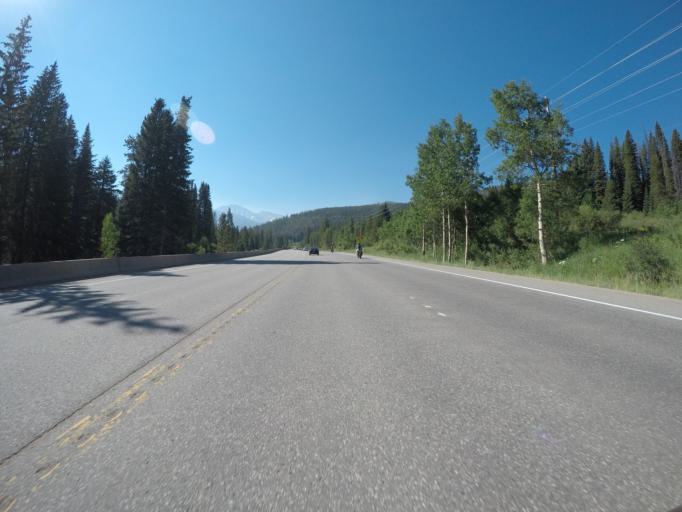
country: US
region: Colorado
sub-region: Grand County
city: Fraser
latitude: 39.9034
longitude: -105.7800
